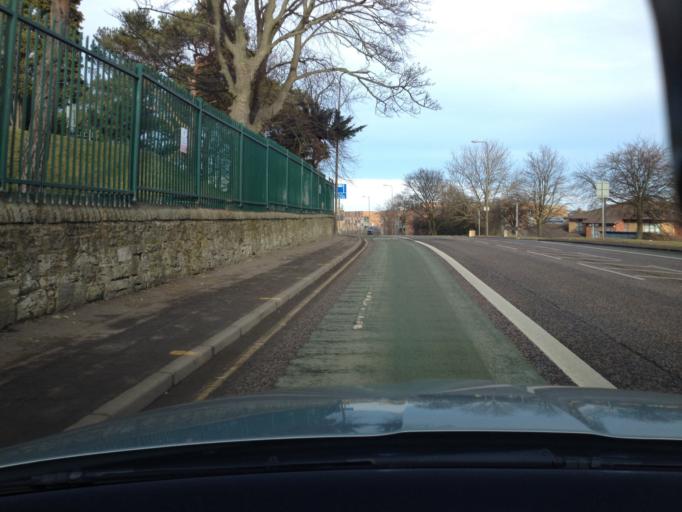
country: GB
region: Scotland
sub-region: Midlothian
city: Loanhead
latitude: 55.9075
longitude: -3.1640
